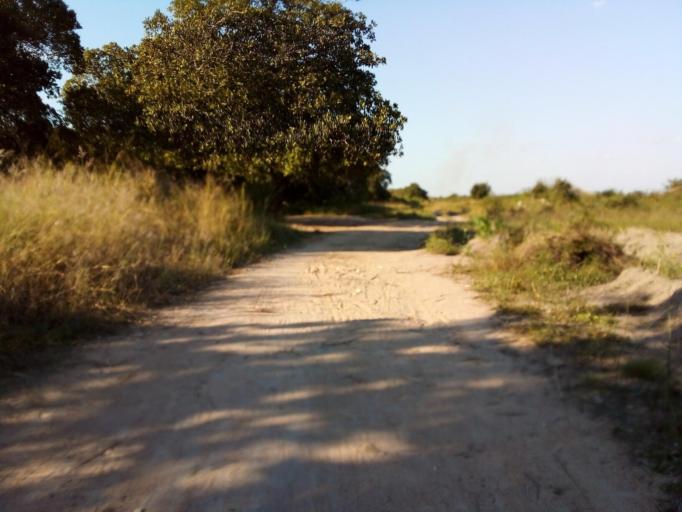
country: MZ
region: Zambezia
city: Quelimane
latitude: -17.5518
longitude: 36.7045
